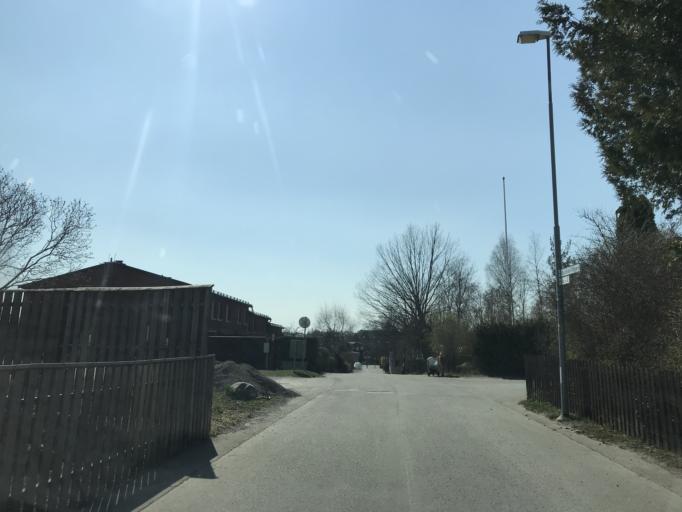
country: SE
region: Stockholm
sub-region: Sollentuna Kommun
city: Sollentuna
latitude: 59.4409
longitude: 17.9449
